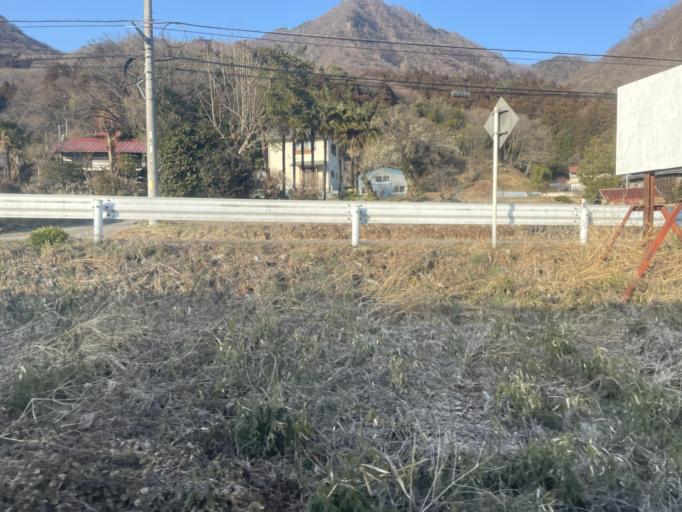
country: JP
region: Gunma
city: Nakanojomachi
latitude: 36.5665
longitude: 138.8900
